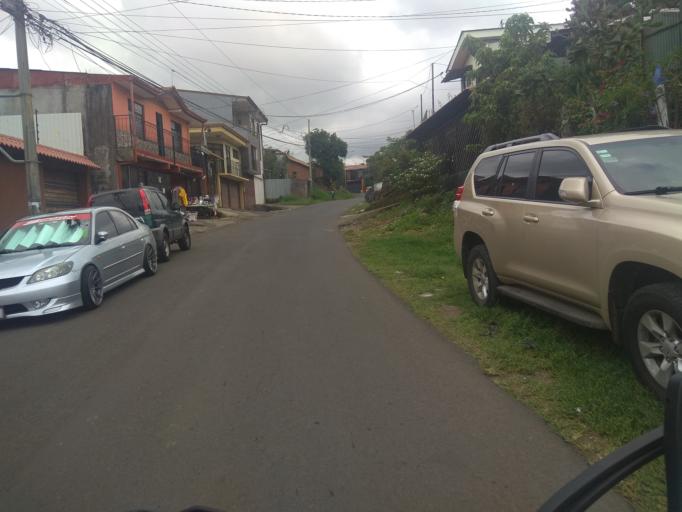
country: CR
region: Heredia
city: San Josecito
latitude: 10.0185
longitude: -84.1031
